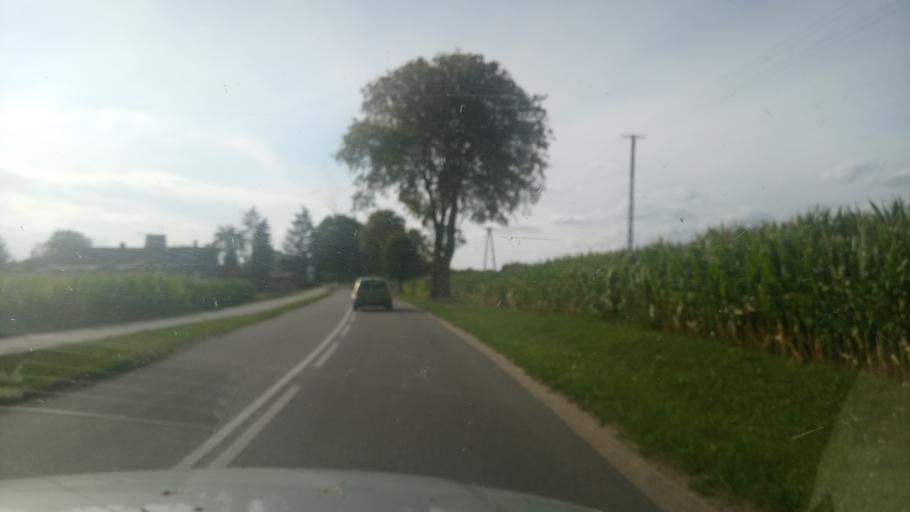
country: PL
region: Greater Poland Voivodeship
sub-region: Powiat pilski
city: Lobzenica
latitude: 53.2532
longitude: 17.2698
